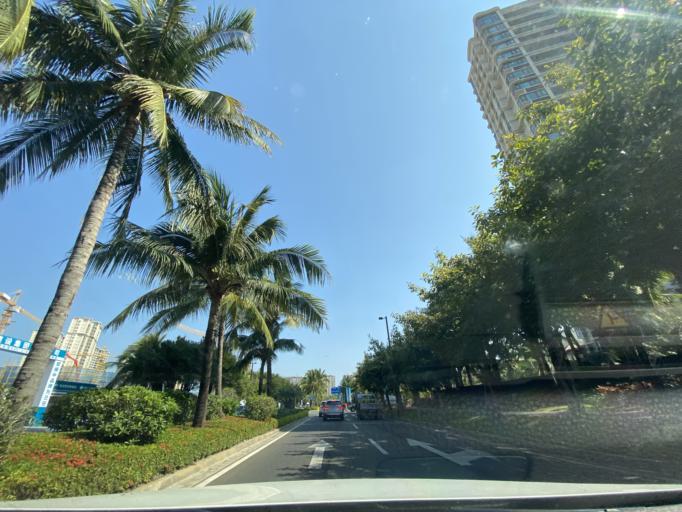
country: CN
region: Hainan
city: Yingzhou
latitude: 18.4071
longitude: 109.8704
